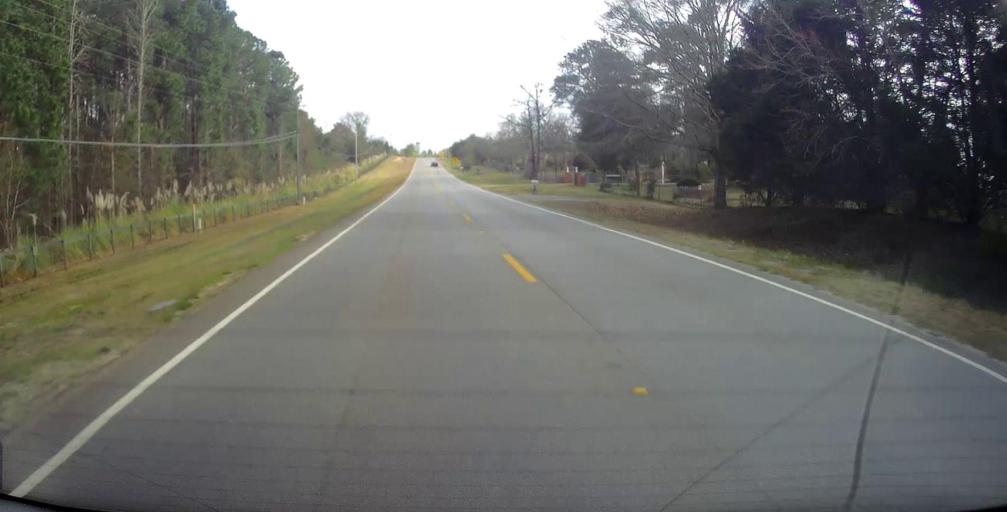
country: US
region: Georgia
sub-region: Marion County
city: Buena Vista
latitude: 32.4557
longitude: -84.5369
